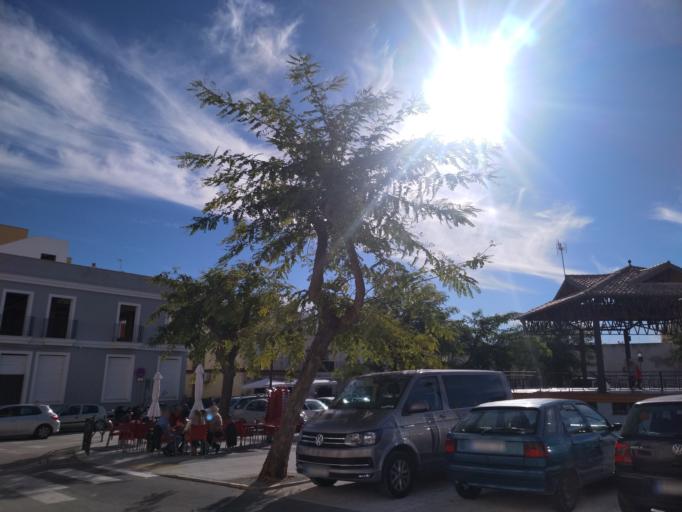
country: ES
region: Andalusia
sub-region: Provincia de Cadiz
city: San Fernando
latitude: 36.4691
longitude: -6.1919
